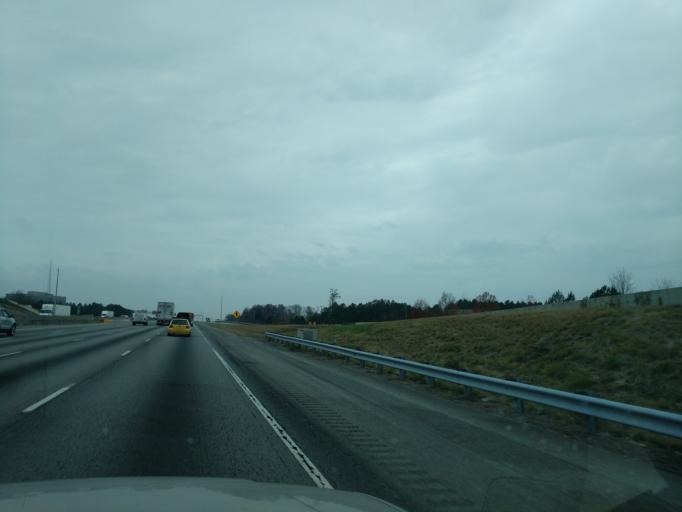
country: US
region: Georgia
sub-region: Gwinnett County
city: Suwanee
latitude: 34.0021
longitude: -84.0739
